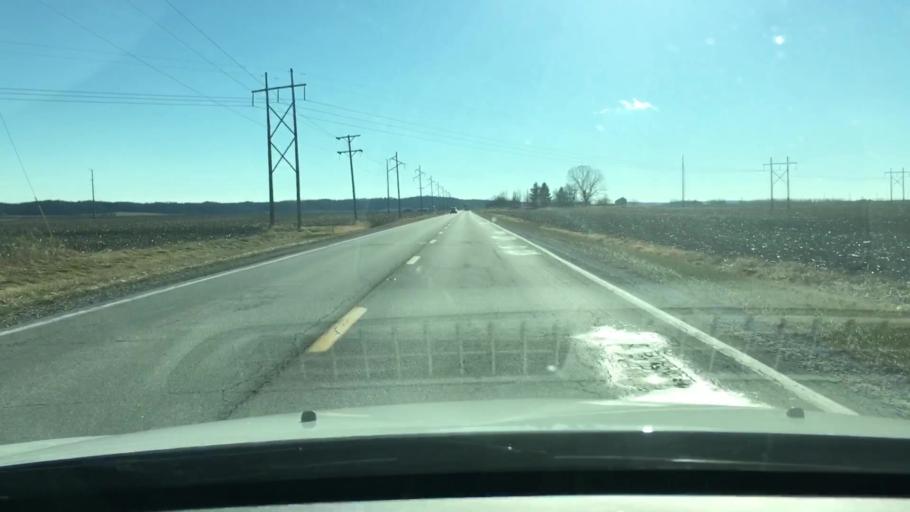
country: US
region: Illinois
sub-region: Morgan County
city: Meredosia
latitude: 39.8685
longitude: -90.5054
